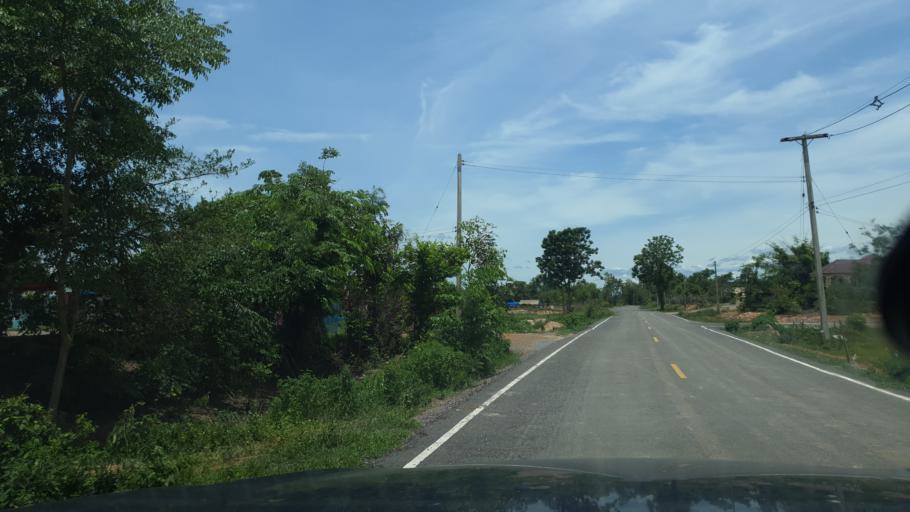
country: TH
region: Sukhothai
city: Ban Na
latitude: 17.1507
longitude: 99.6648
